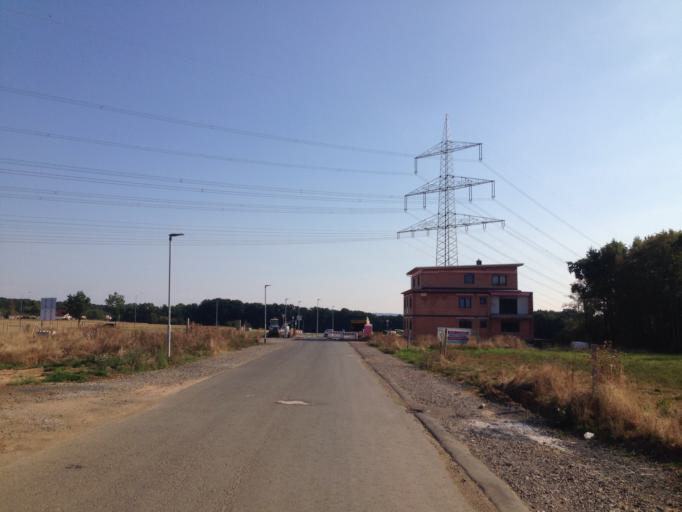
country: DE
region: Hesse
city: Allendorf an der Lahn
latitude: 50.5558
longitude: 8.6304
